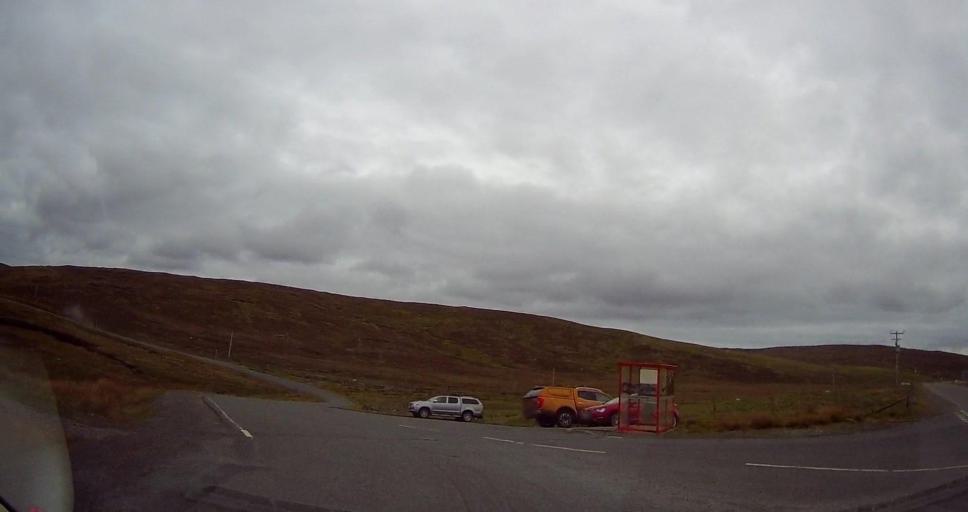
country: GB
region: Scotland
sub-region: Shetland Islands
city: Shetland
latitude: 60.6056
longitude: -1.0912
